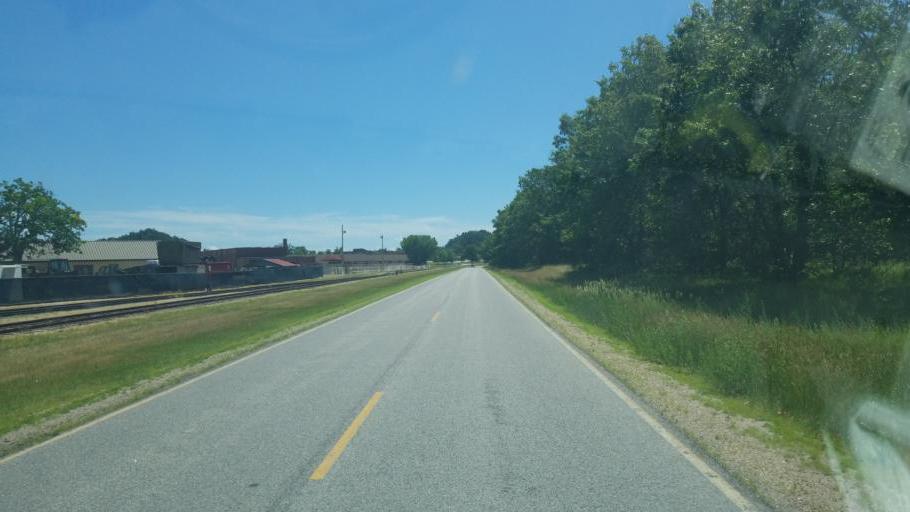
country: US
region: Wisconsin
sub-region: Juneau County
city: New Lisbon
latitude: 43.9301
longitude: -90.2752
